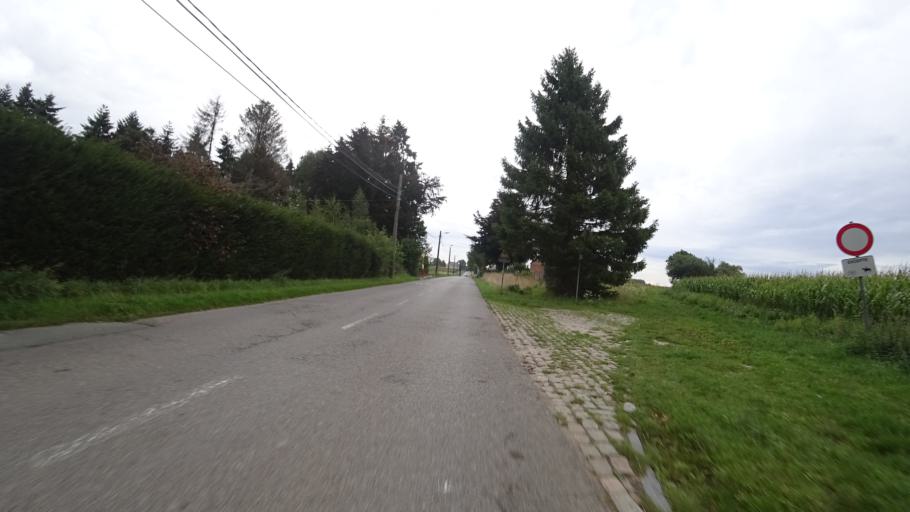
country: BE
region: Wallonia
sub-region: Province du Brabant Wallon
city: Walhain-Saint-Paul
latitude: 50.6152
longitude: 4.7048
